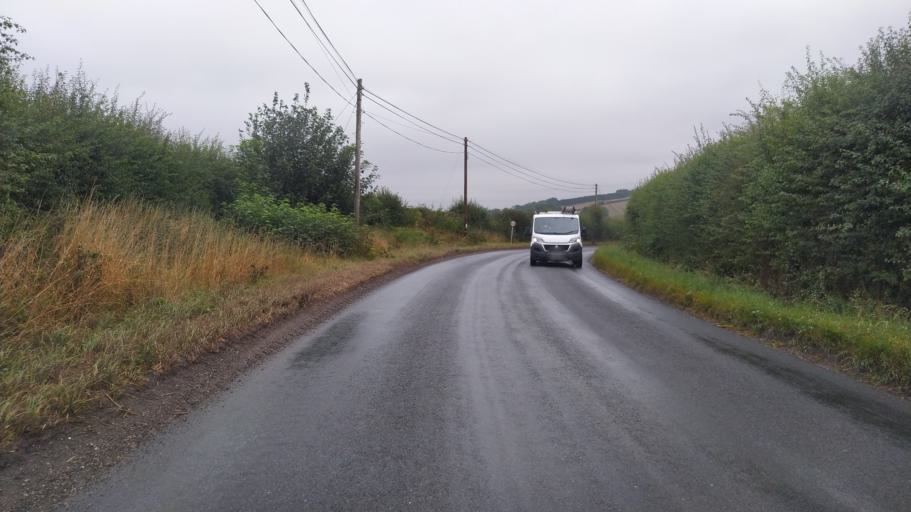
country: GB
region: England
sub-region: Wiltshire
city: Bishopstone
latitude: 51.0395
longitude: -1.8664
